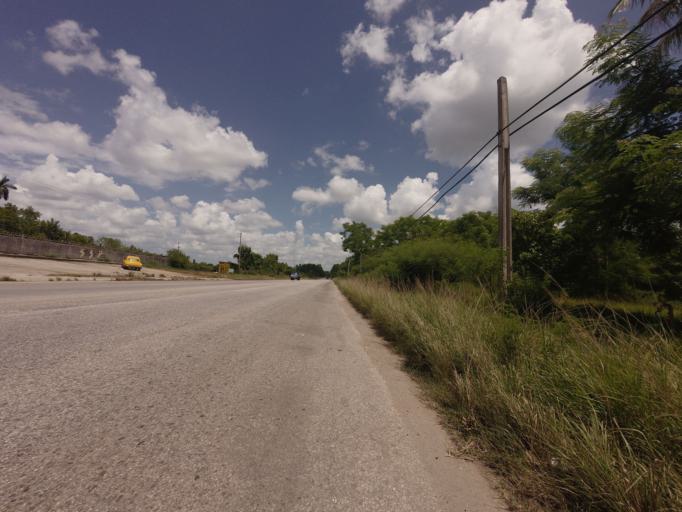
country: CU
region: La Habana
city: Arroyo Naranjo
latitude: 23.0363
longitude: -82.3469
